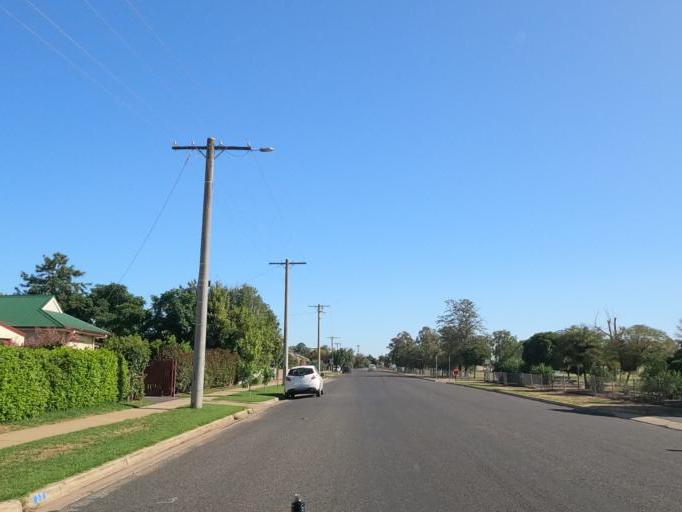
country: AU
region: Victoria
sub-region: Moira
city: Yarrawonga
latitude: -36.0218
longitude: 146.0054
